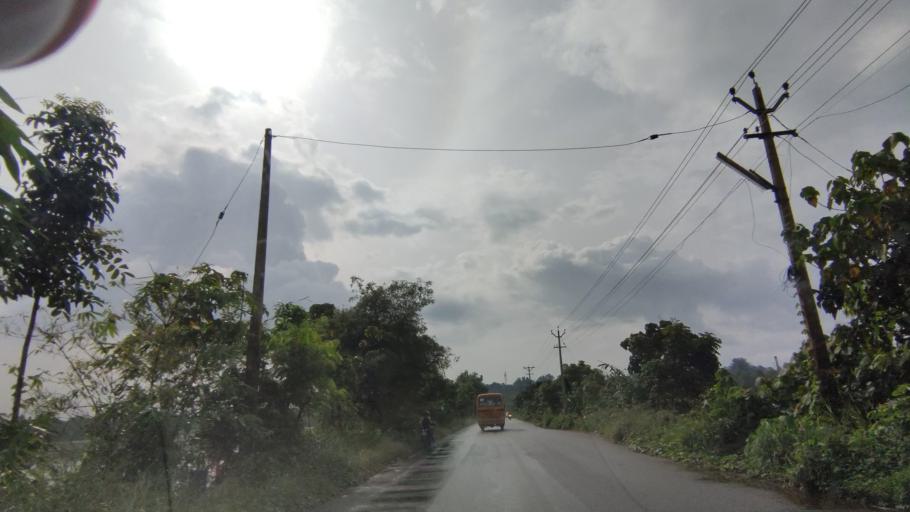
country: IN
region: Kerala
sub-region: Kottayam
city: Kottayam
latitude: 9.5645
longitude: 76.5083
